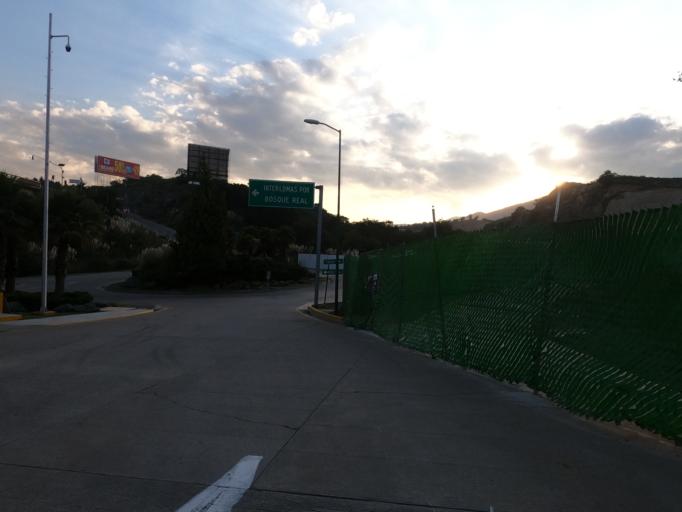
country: MX
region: Mexico
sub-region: Naucalpan de Juarez
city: Ejido el Castillo
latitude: 19.4214
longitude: -99.2997
